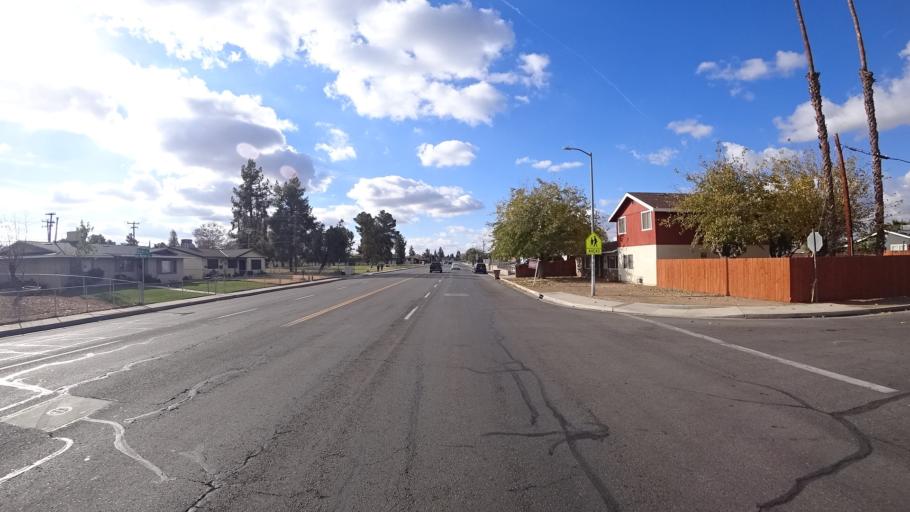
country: US
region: California
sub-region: Kern County
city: Bakersfield
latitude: 35.3323
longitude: -119.0495
